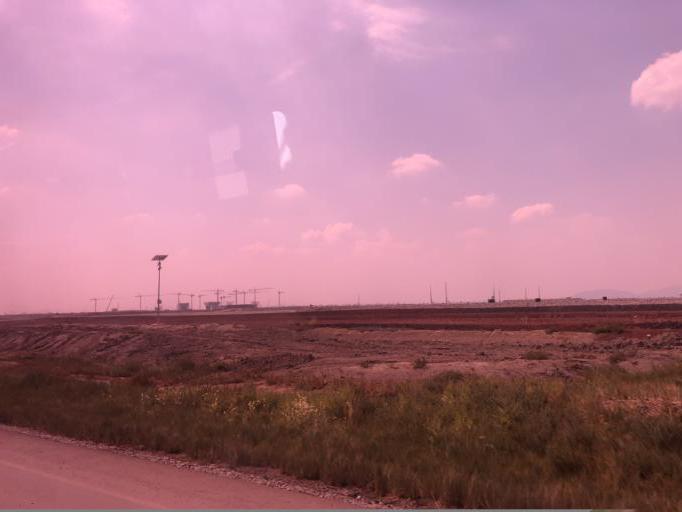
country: MX
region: Mexico
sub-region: Texcoco
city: Colonia Lazaro Cardenas
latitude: 19.5154
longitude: -98.9860
